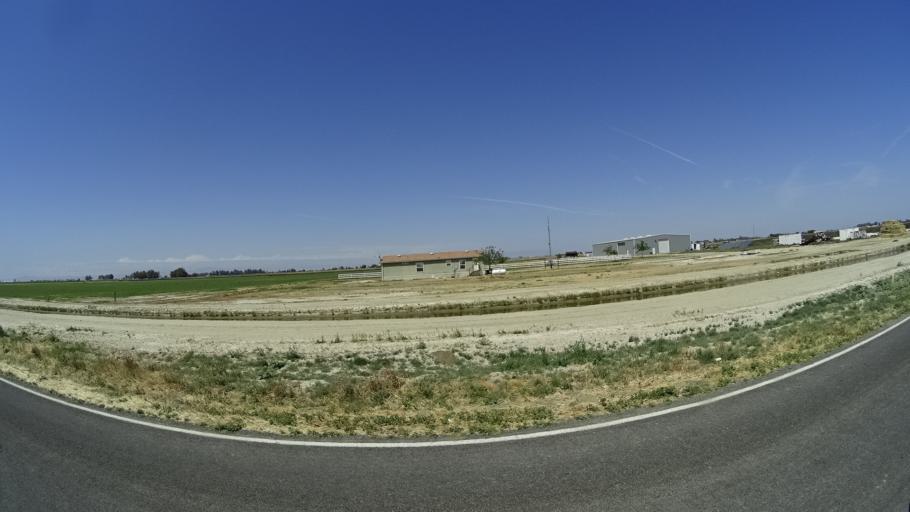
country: US
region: California
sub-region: Kings County
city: Stratford
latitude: 36.2138
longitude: -119.7624
